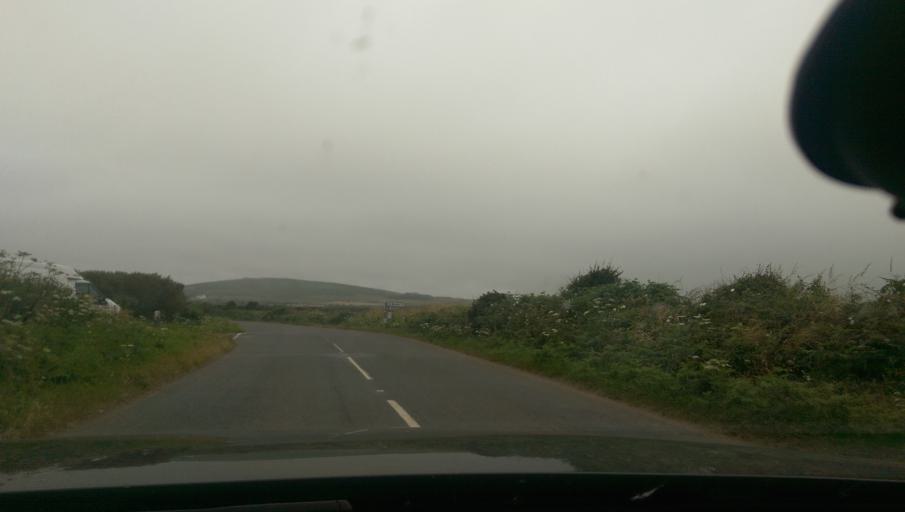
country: GB
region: England
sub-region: Cornwall
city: St. Buryan
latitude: 50.0910
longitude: -5.6361
